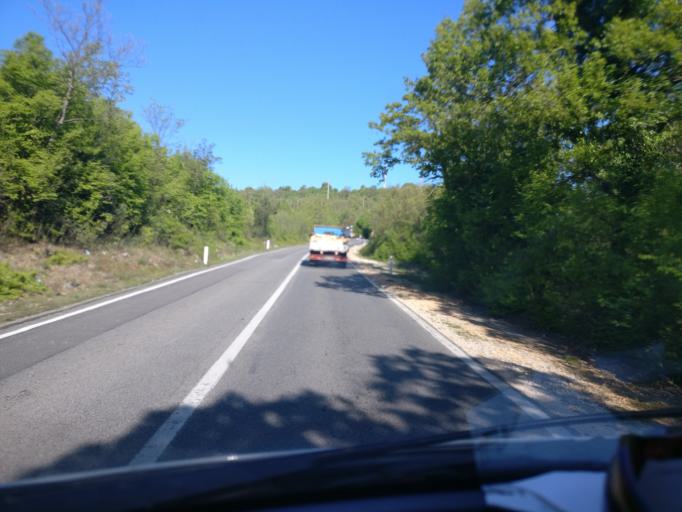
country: BA
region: Federation of Bosnia and Herzegovina
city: Crnici
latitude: 43.1016
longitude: 17.9067
